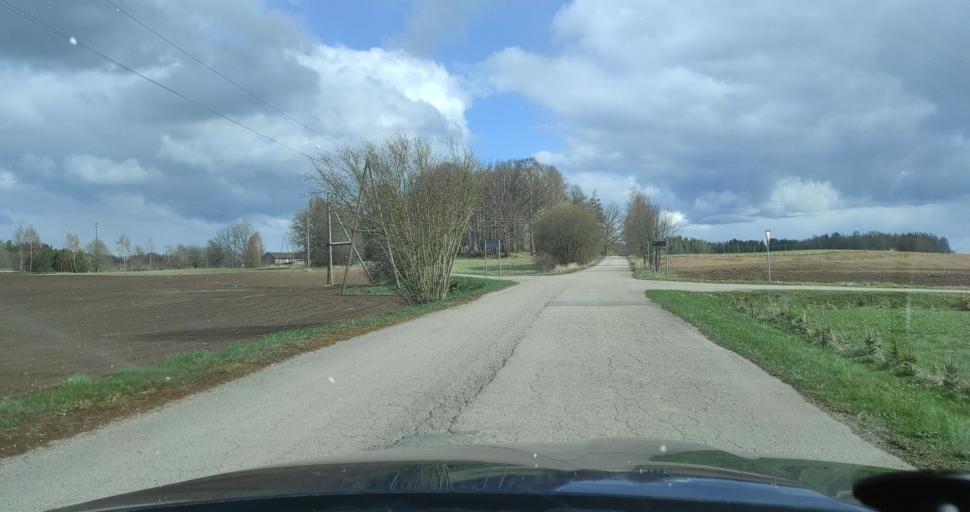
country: LV
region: Aizpute
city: Aizpute
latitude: 56.7127
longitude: 21.5764
